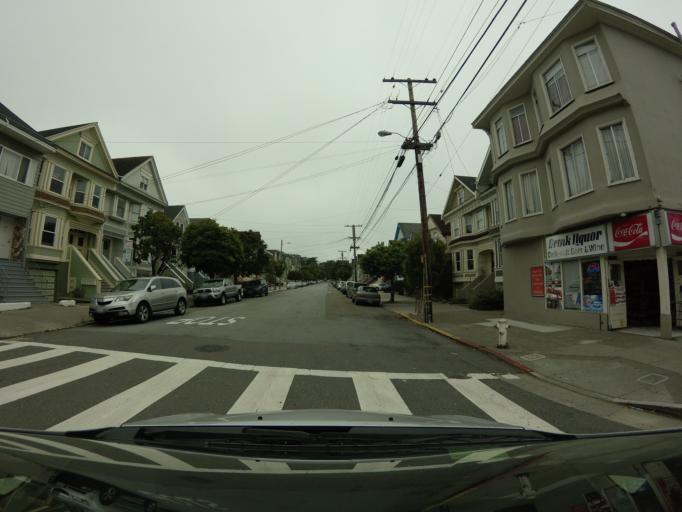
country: US
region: California
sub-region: San Francisco County
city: San Francisco
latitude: 37.7774
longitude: -122.4598
